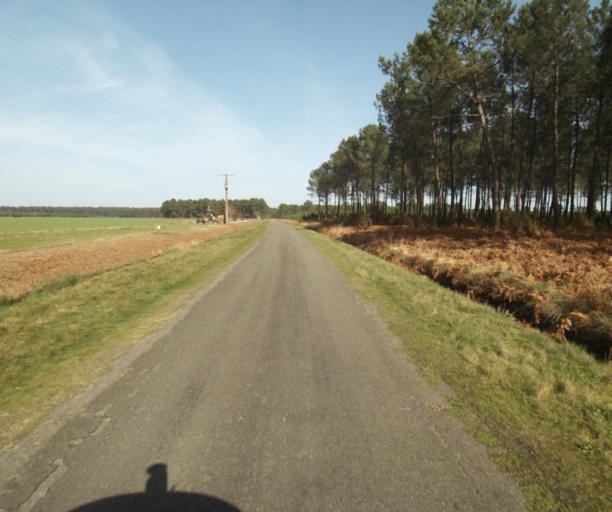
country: FR
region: Aquitaine
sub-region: Departement des Landes
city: Roquefort
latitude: 44.1693
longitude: -0.1971
